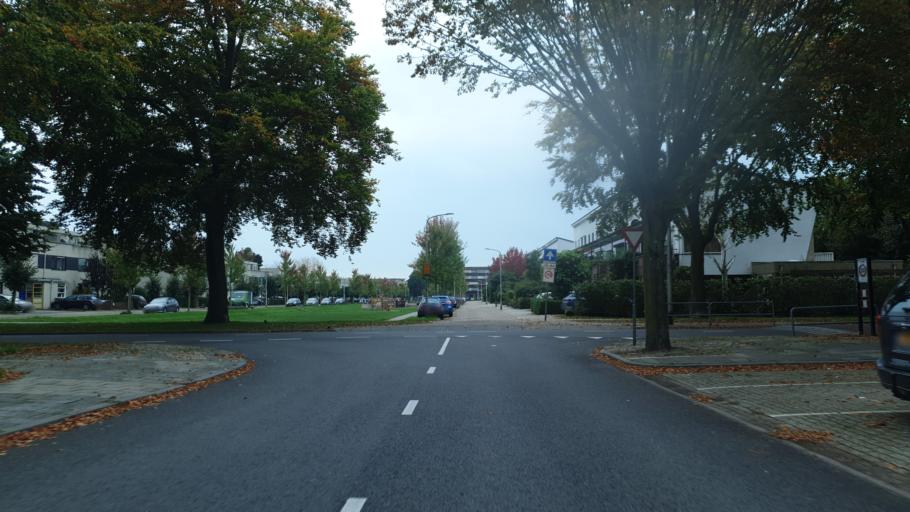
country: NL
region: Gelderland
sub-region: Gemeente Nijmegen
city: Nijmegen
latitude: 51.8106
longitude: 5.8393
